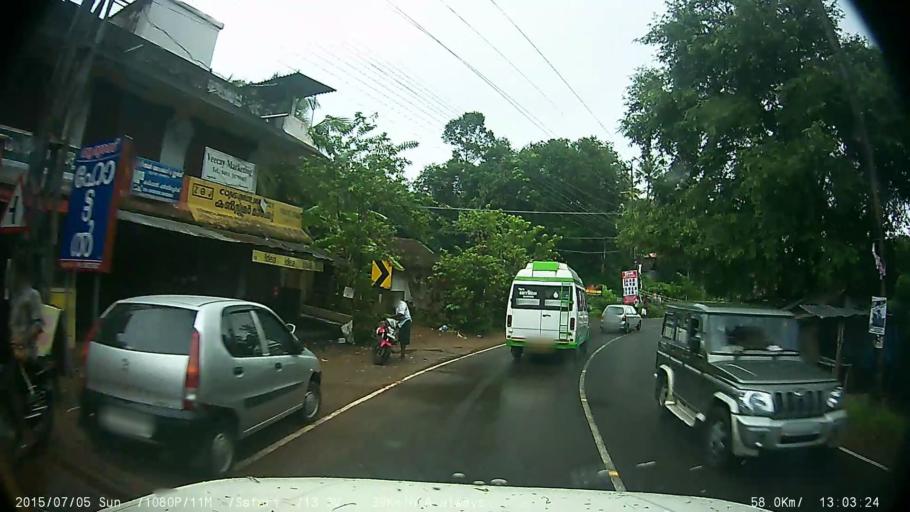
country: IN
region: Kerala
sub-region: Kottayam
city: Changanacheri
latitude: 9.4976
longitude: 76.5726
